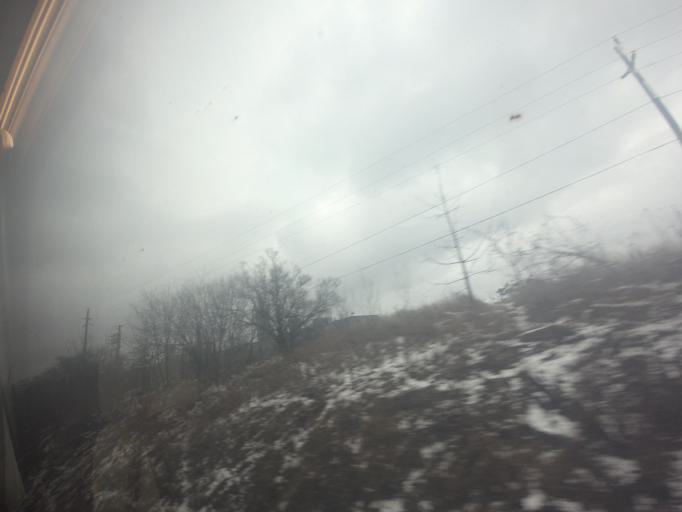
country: CA
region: Ontario
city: Cobourg
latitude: 43.9491
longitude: -78.2835
